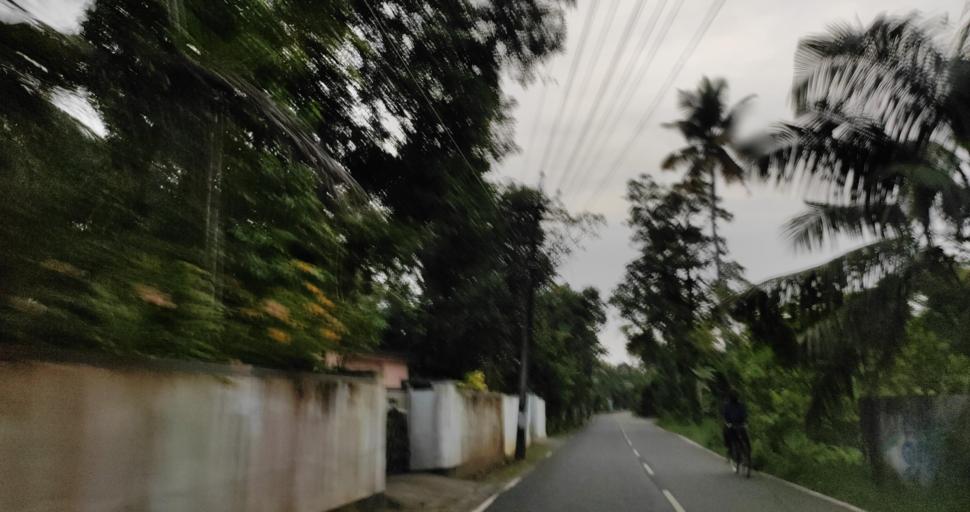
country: IN
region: Kerala
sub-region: Alappuzha
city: Vayalar
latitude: 9.6809
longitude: 76.3237
